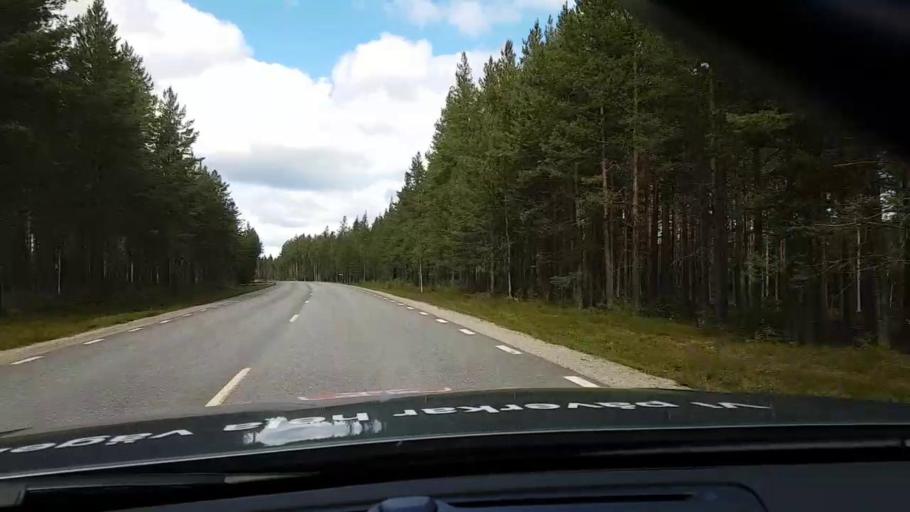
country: SE
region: Vaesternorrland
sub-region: OErnskoeldsviks Kommun
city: Bredbyn
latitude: 63.5355
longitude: 17.9657
